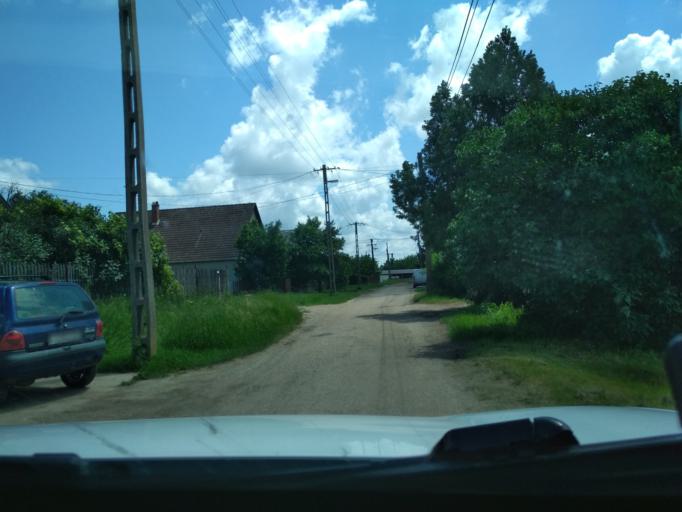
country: HU
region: Jasz-Nagykun-Szolnok
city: Tiszafured
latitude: 47.6003
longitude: 20.7556
